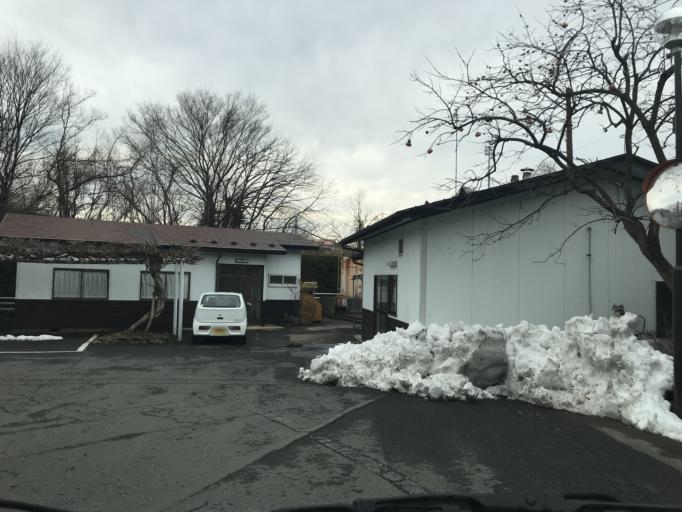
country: JP
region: Iwate
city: Mizusawa
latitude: 39.1725
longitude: 141.1390
